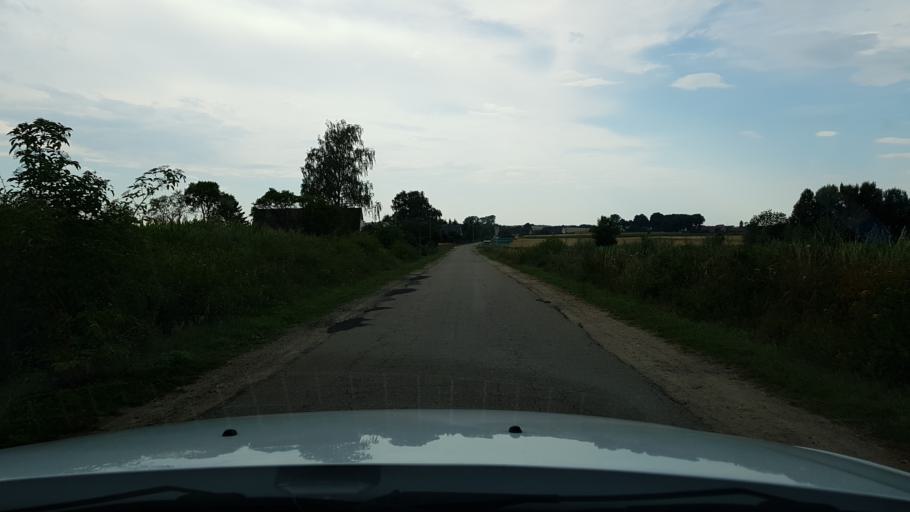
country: PL
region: West Pomeranian Voivodeship
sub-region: Powiat walecki
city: Walcz
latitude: 53.3720
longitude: 16.3297
